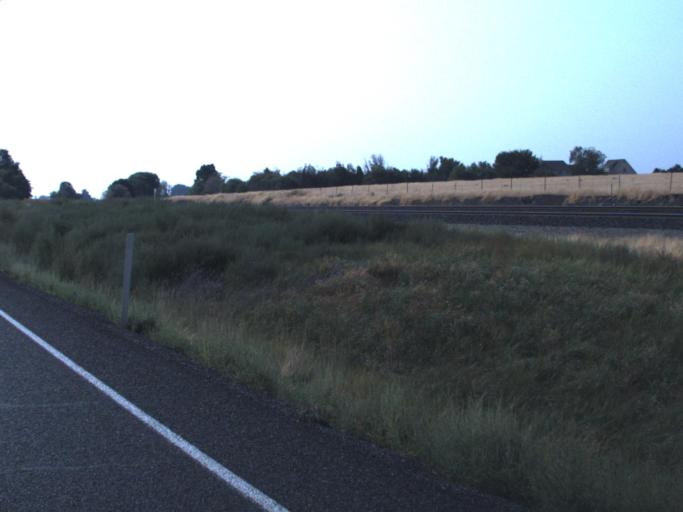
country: US
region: Washington
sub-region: Yakima County
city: Grandview
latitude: 46.1859
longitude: -119.8534
